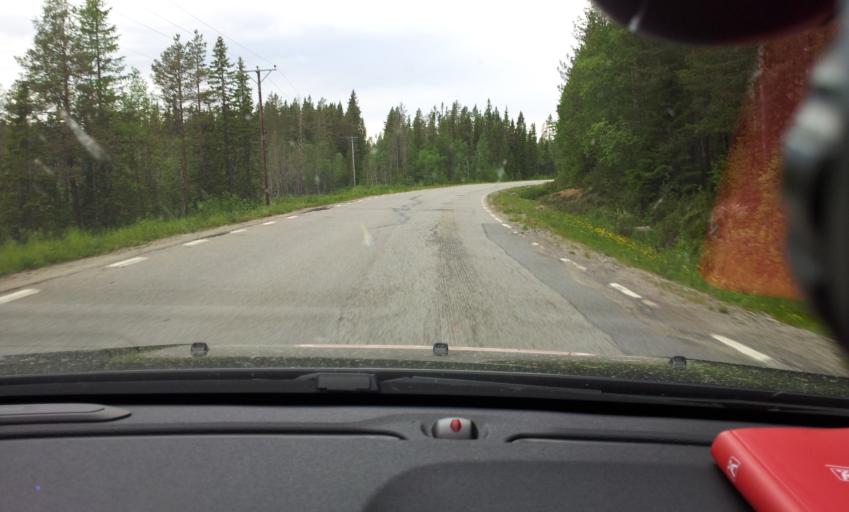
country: SE
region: Jaemtland
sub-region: Bergs Kommun
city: Hoverberg
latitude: 62.6824
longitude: 14.6473
